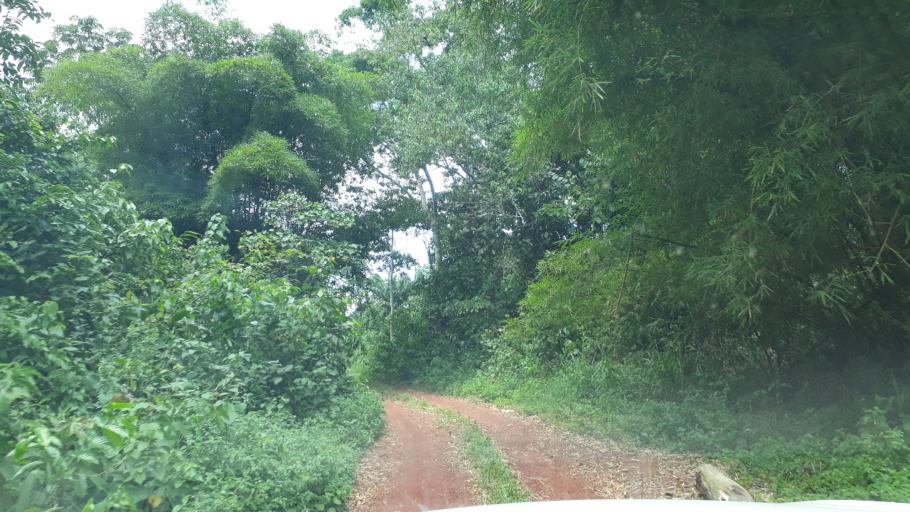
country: CD
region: Eastern Province
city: Kisangani
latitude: 0.4792
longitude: 25.5126
